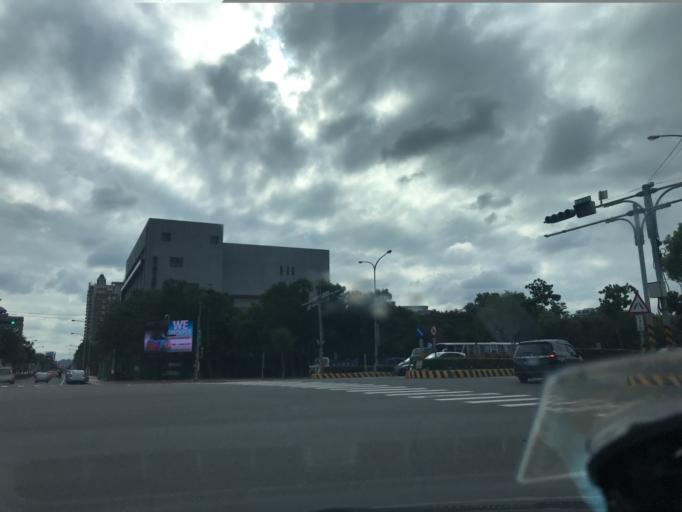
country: TW
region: Taiwan
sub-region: Hsinchu
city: Zhubei
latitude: 24.8220
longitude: 121.0227
